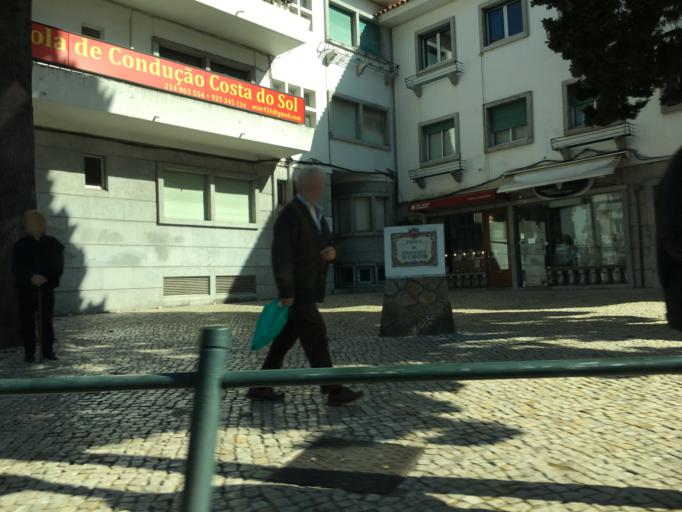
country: PT
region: Lisbon
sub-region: Cascais
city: Cascais
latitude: 38.7007
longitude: -9.4204
